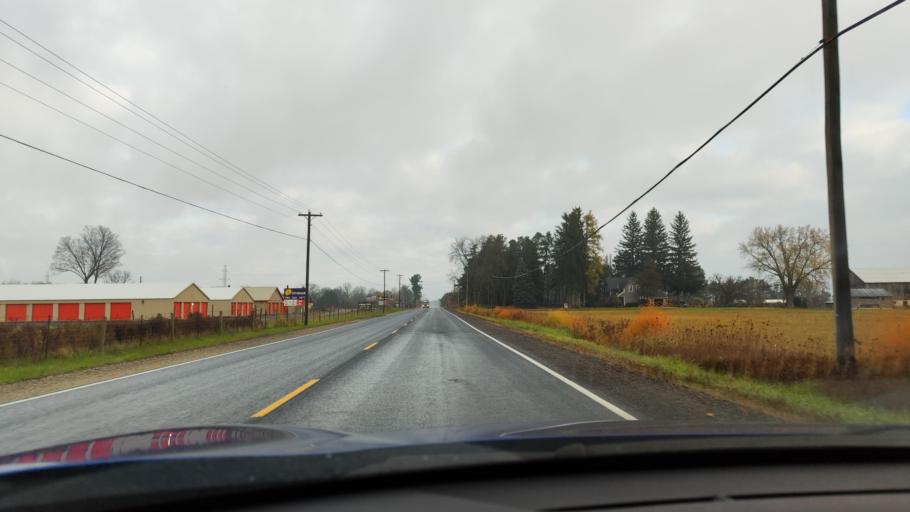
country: CA
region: Ontario
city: Angus
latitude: 44.3559
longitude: -79.9402
